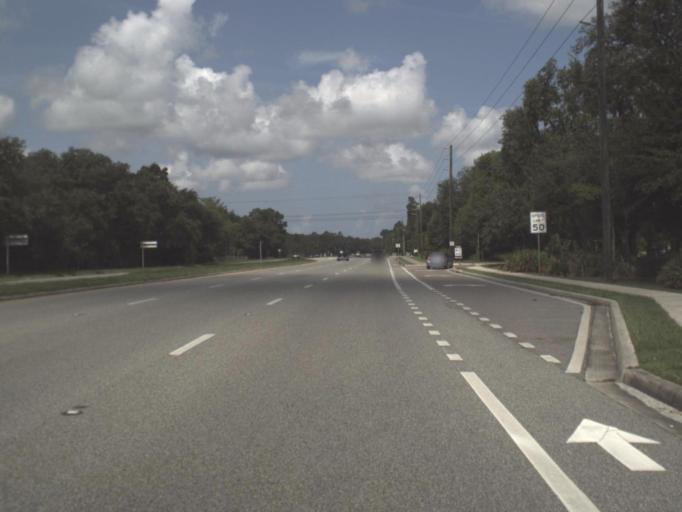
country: US
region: Florida
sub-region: Pasco County
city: Shady Hills
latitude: 28.3298
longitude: -82.5701
